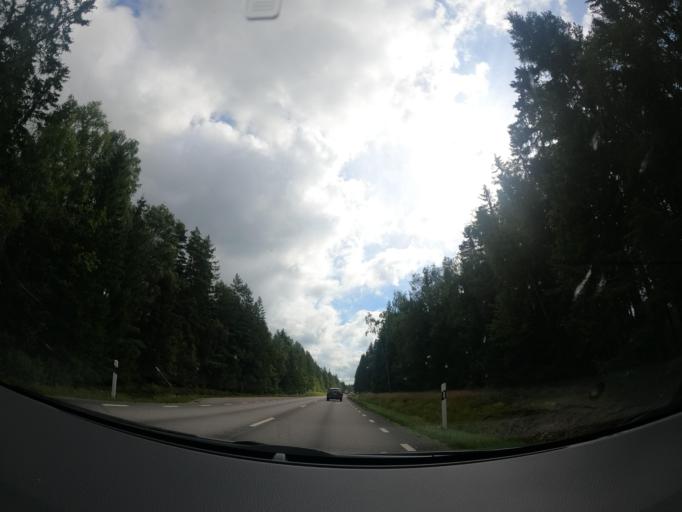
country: SE
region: Joenkoeping
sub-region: Gislaveds Kommun
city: Smalandsstenar
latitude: 57.1261
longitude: 13.3310
